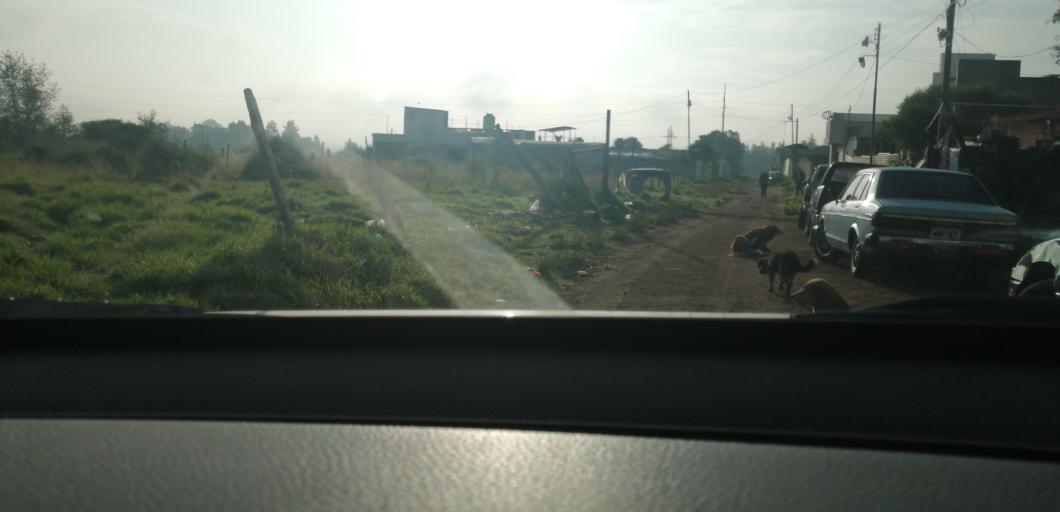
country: GT
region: Quetzaltenango
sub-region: Municipio de La Esperanza
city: La Esperanza
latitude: 14.8680
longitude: -91.5469
